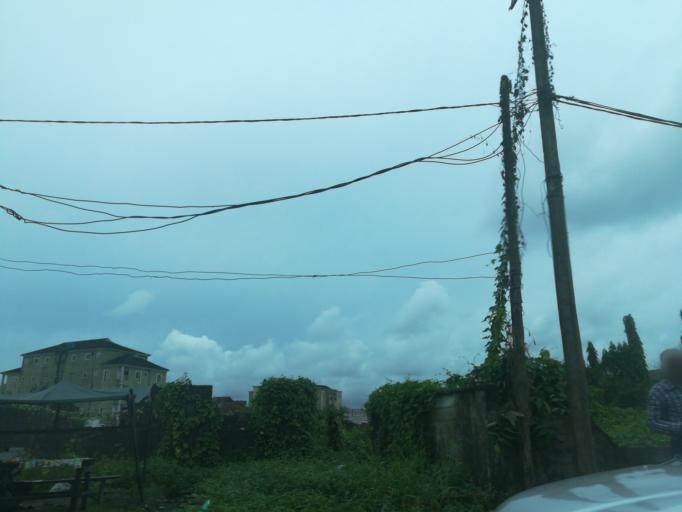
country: NG
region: Rivers
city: Port Harcourt
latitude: 4.8215
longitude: 6.9902
